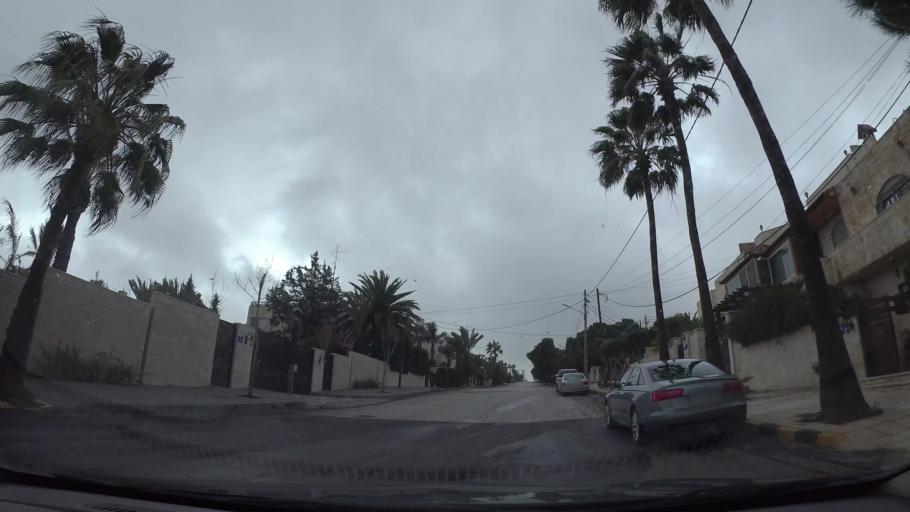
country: JO
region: Amman
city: Al Bunayyat ash Shamaliyah
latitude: 31.9399
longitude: 35.8827
